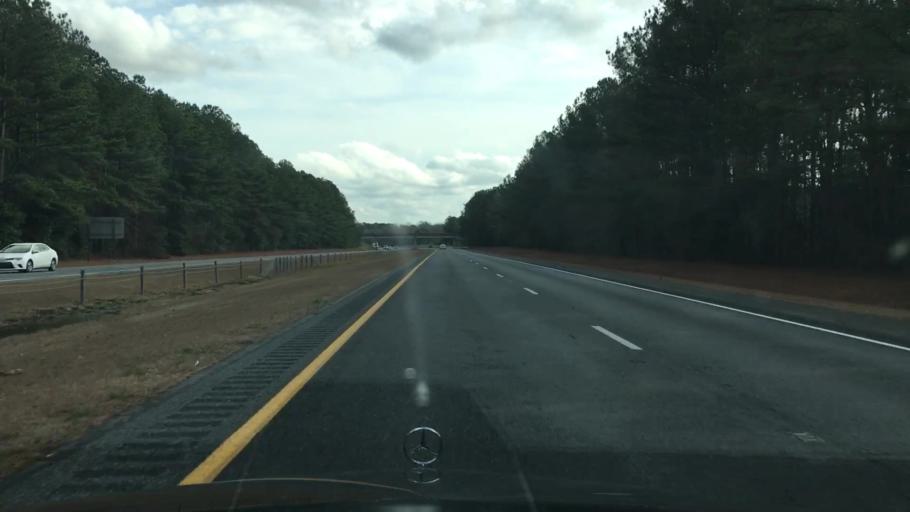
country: US
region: North Carolina
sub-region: Sampson County
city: Clinton
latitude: 35.2170
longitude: -78.3321
